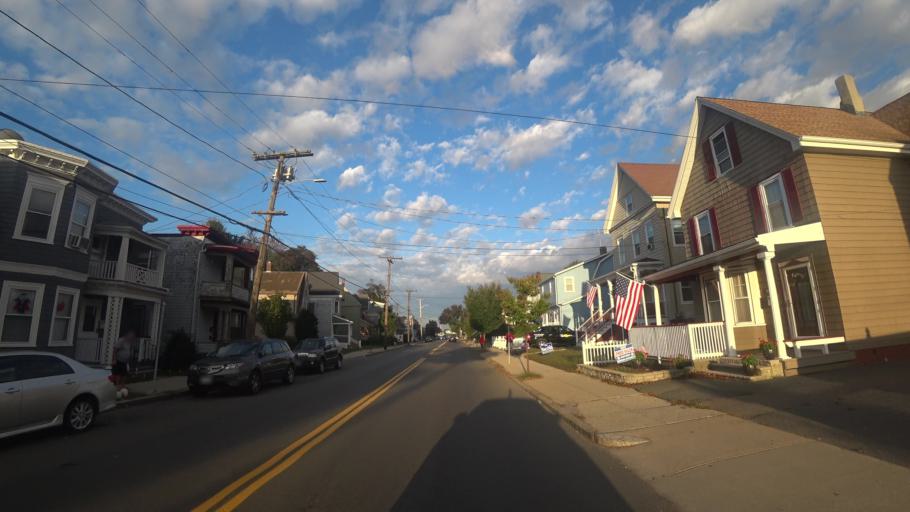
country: US
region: Massachusetts
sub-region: Suffolk County
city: Winthrop
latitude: 42.3822
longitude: -70.9879
